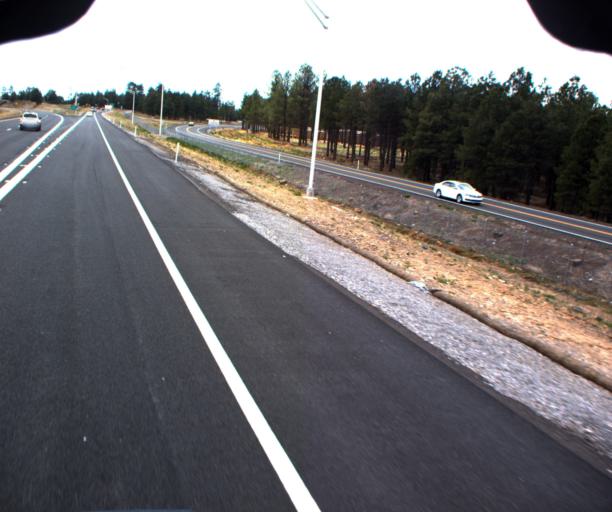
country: US
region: Arizona
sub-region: Coconino County
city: Kachina Village
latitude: 35.1452
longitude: -111.6837
